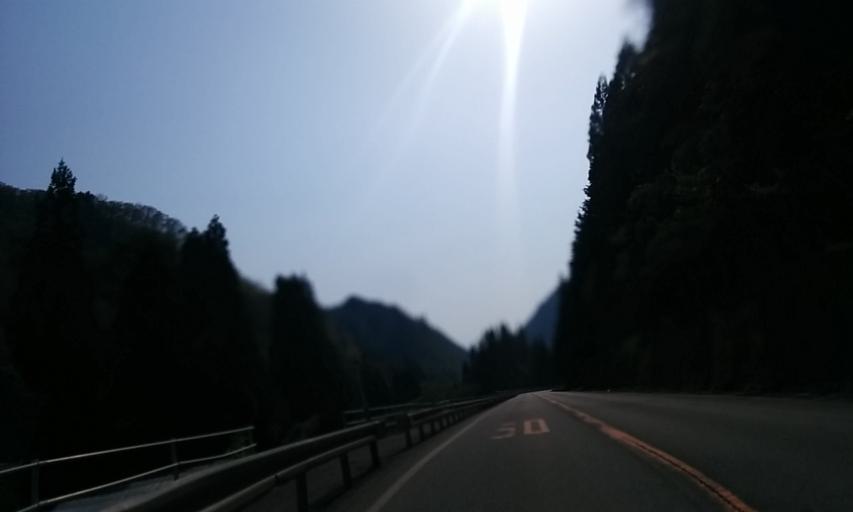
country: JP
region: Gifu
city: Takayama
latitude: 36.1756
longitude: 137.3799
